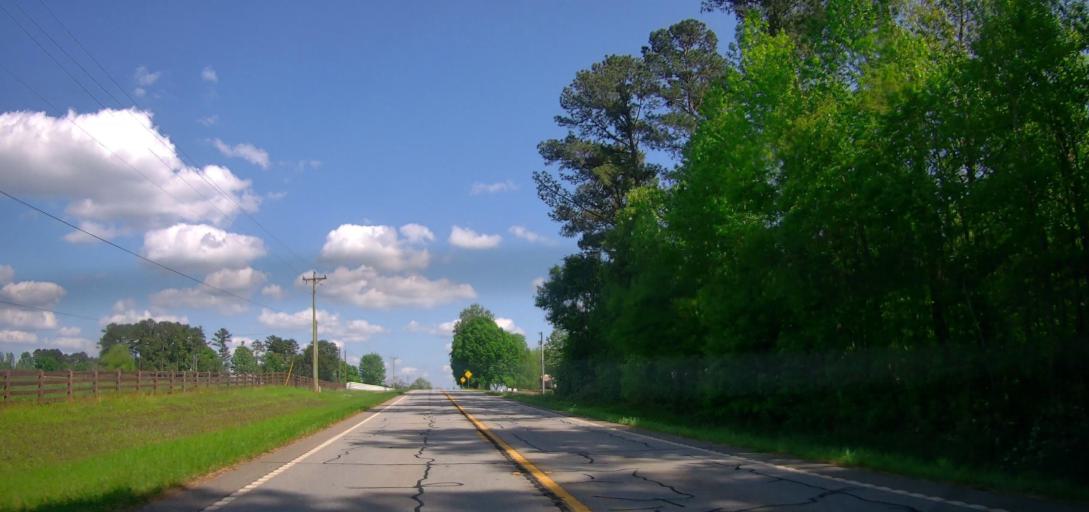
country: US
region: Georgia
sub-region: Greene County
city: Greensboro
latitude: 33.6138
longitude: -83.3176
